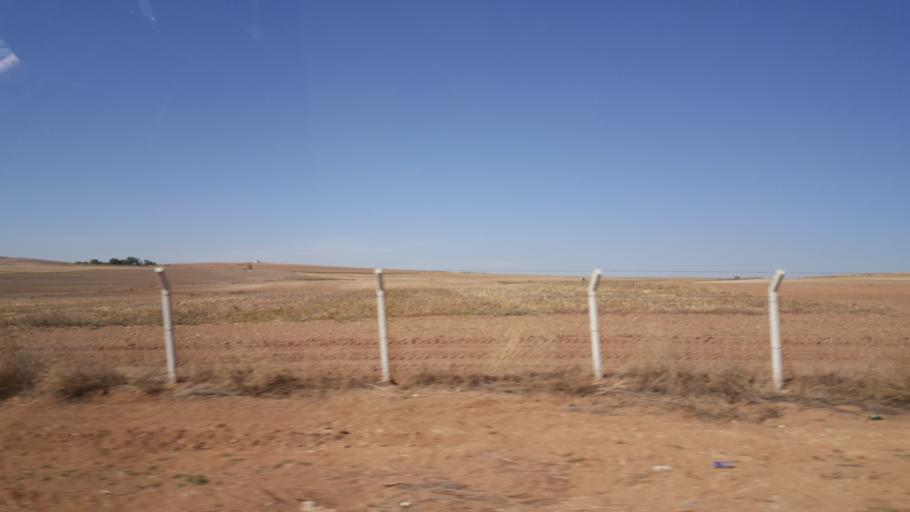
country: TR
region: Ankara
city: Ikizce
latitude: 39.6187
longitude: 32.6910
